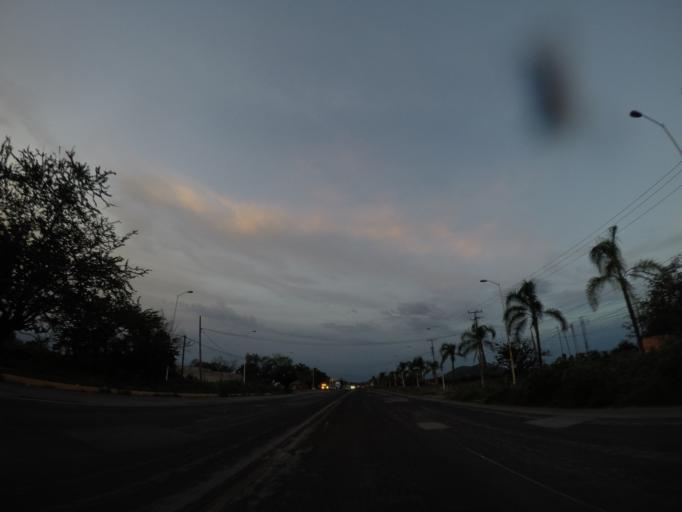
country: MX
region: Morelos
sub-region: Jojutla
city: Tehuixtla
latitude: 18.5920
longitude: -99.2588
